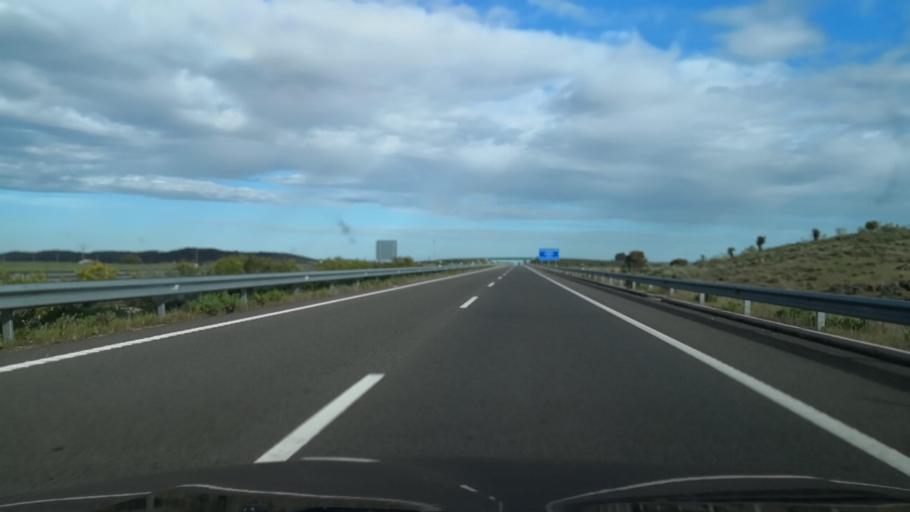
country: ES
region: Extremadura
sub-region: Provincia de Caceres
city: Casas de Don Gomez
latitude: 40.0212
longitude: -6.5956
